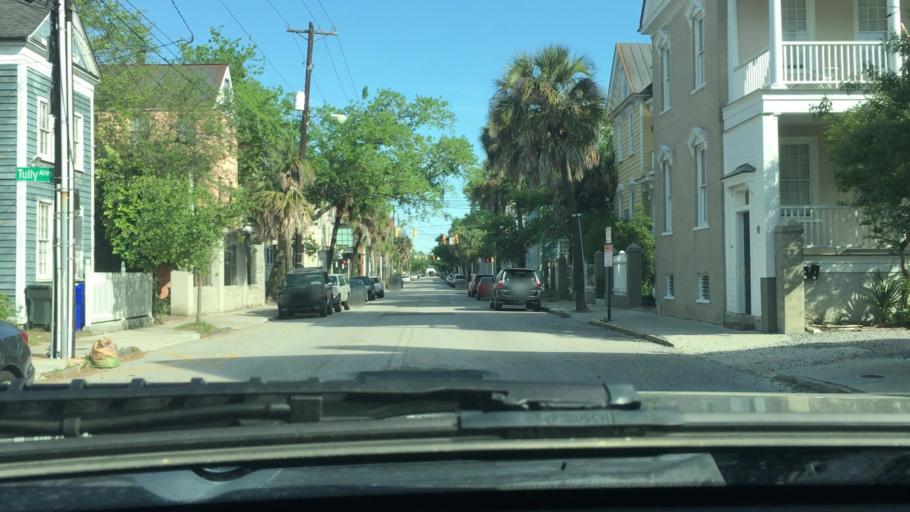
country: US
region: South Carolina
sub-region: Charleston County
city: Charleston
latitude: 32.7908
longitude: -79.9414
